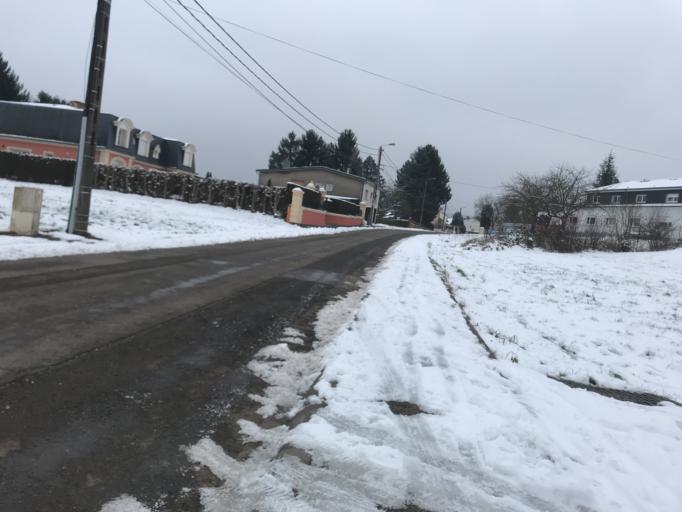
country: FR
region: Lorraine
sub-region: Departement de la Moselle
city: Russange
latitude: 49.4892
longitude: 5.9479
